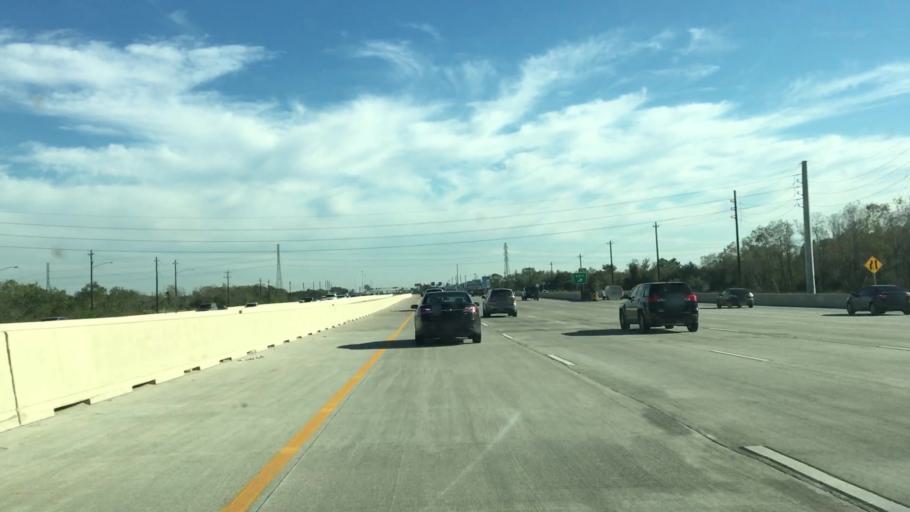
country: US
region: Texas
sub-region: Galveston County
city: Friendswood
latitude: 29.5667
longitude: -95.1667
